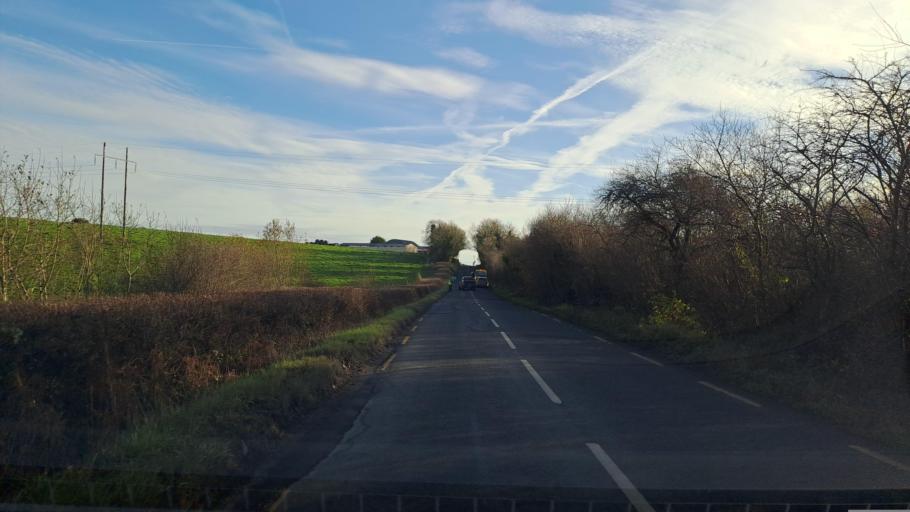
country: IE
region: Ulster
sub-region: An Cabhan
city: Kingscourt
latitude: 53.8795
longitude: -6.7268
